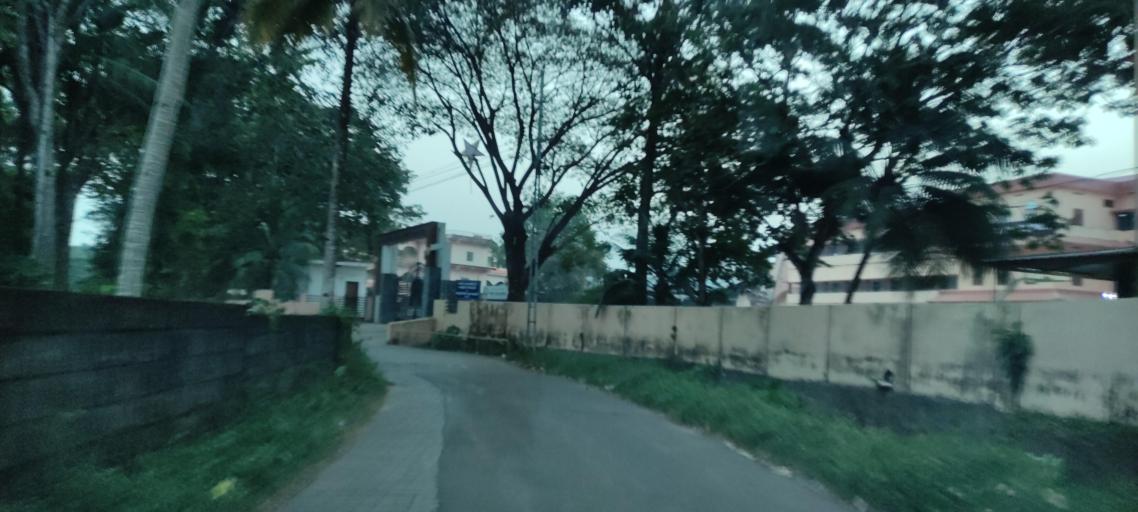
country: IN
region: Kerala
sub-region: Pattanamtitta
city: Adur
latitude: 9.1593
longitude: 76.7385
